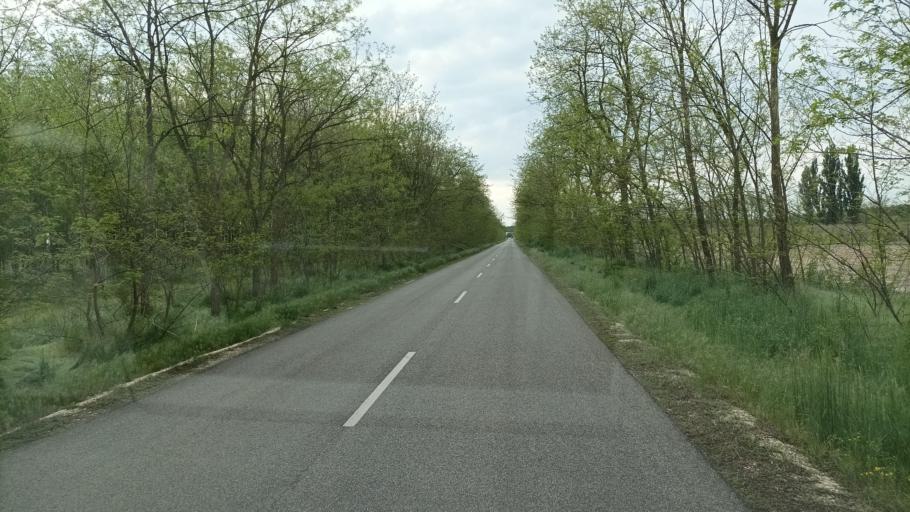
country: HU
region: Pest
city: Monor
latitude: 47.3066
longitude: 19.4253
